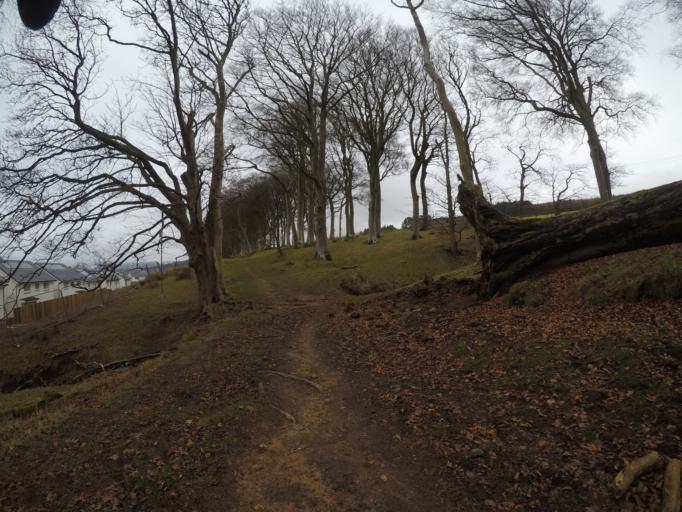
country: GB
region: Scotland
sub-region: North Ayrshire
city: Fairlie
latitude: 55.7579
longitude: -4.8497
